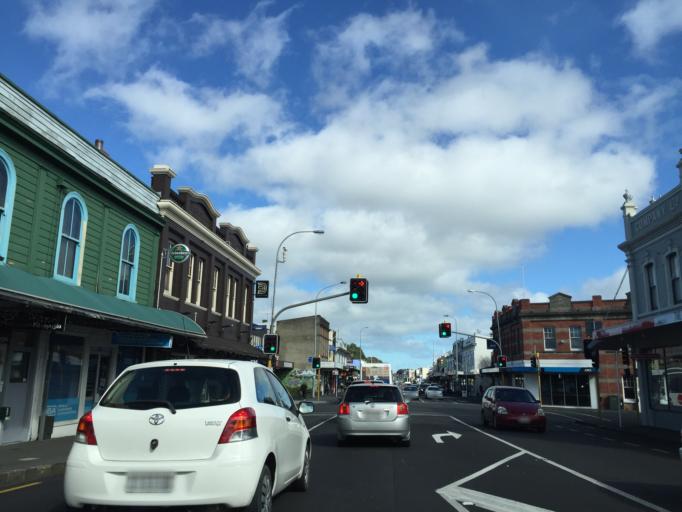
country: NZ
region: Auckland
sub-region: Auckland
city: Auckland
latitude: -36.8756
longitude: 174.7512
